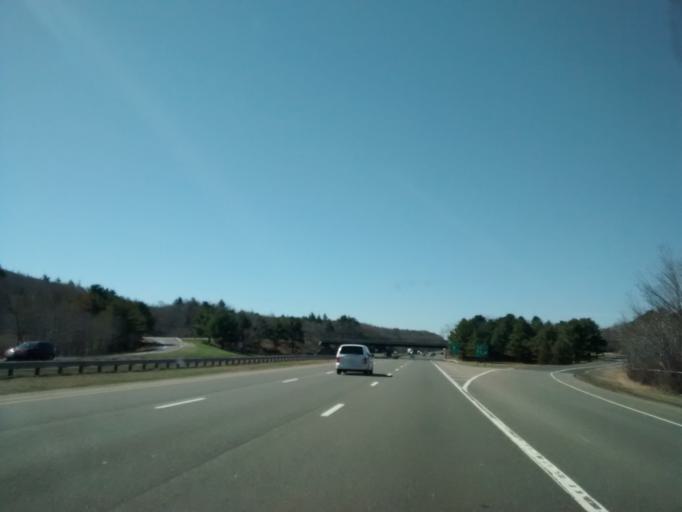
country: US
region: Massachusetts
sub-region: Hampden County
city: Holland
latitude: 41.9785
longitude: -72.1812
